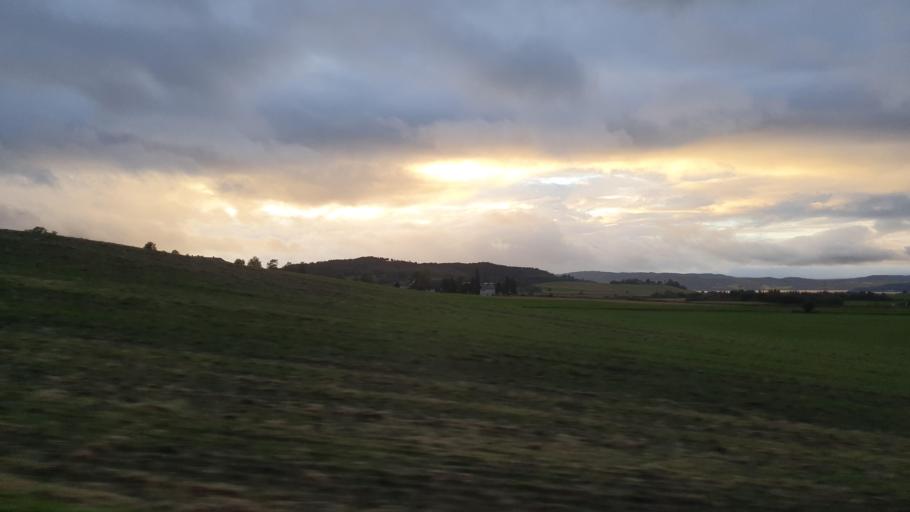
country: NO
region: Nord-Trondelag
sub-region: Levanger
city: Skogn
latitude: 63.6863
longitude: 11.1790
